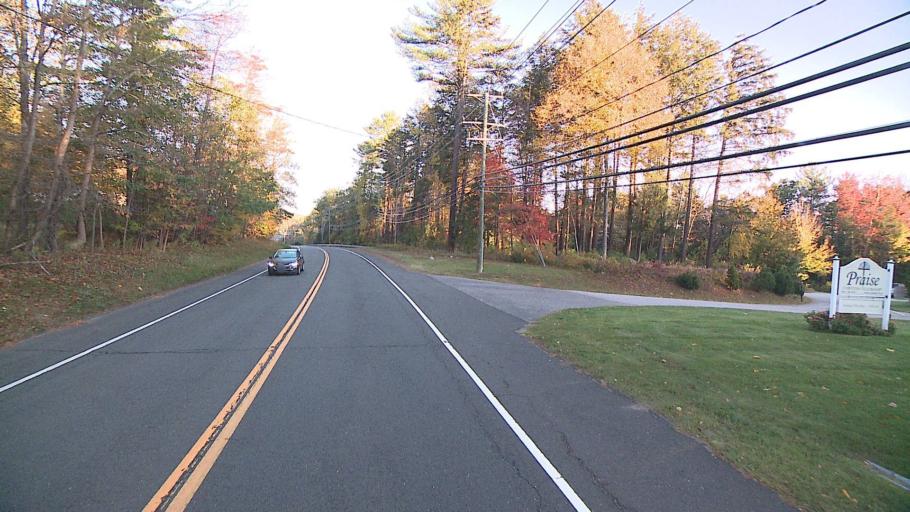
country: US
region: Connecticut
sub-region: Litchfield County
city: New Hartford Center
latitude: 41.9000
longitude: -72.9922
